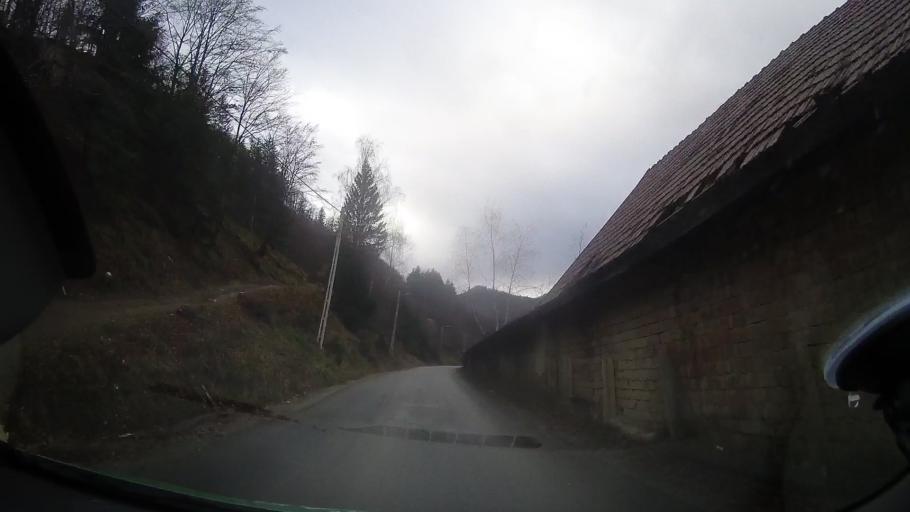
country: RO
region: Cluj
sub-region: Comuna Valea Ierii
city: Valea Ierii
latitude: 46.6448
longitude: 23.3312
